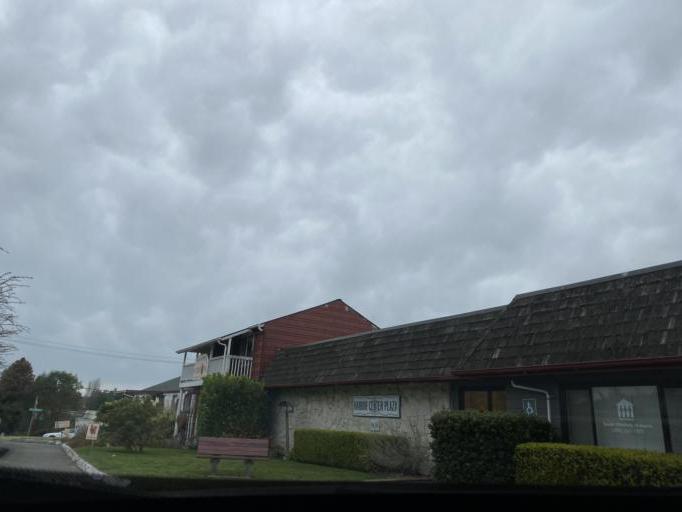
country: US
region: Washington
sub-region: Island County
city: Freeland
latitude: 48.0097
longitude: -122.5264
